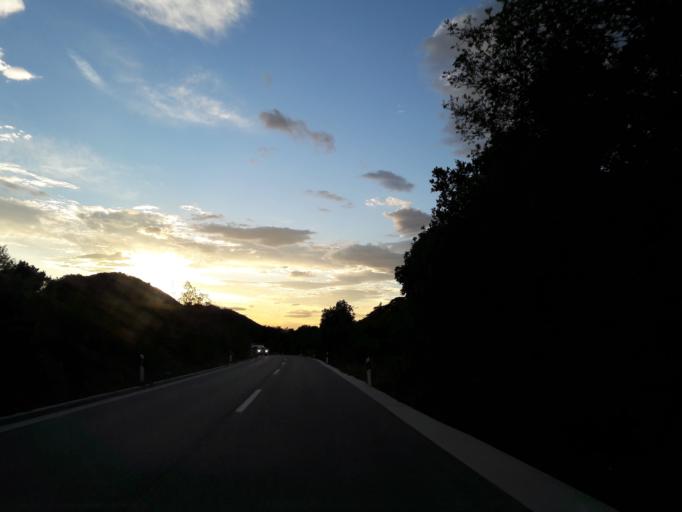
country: HR
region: Dubrovacko-Neretvanska
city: Orebic
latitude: 42.9607
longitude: 17.3169
